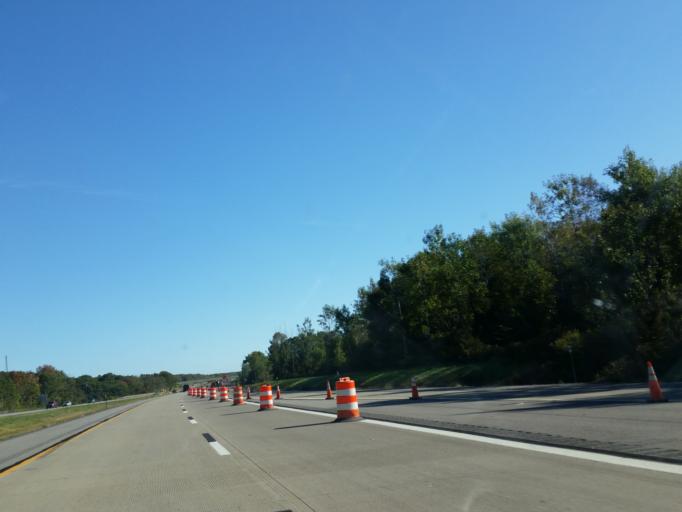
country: US
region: New York
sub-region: Erie County
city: Eden
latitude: 42.6889
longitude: -78.9356
